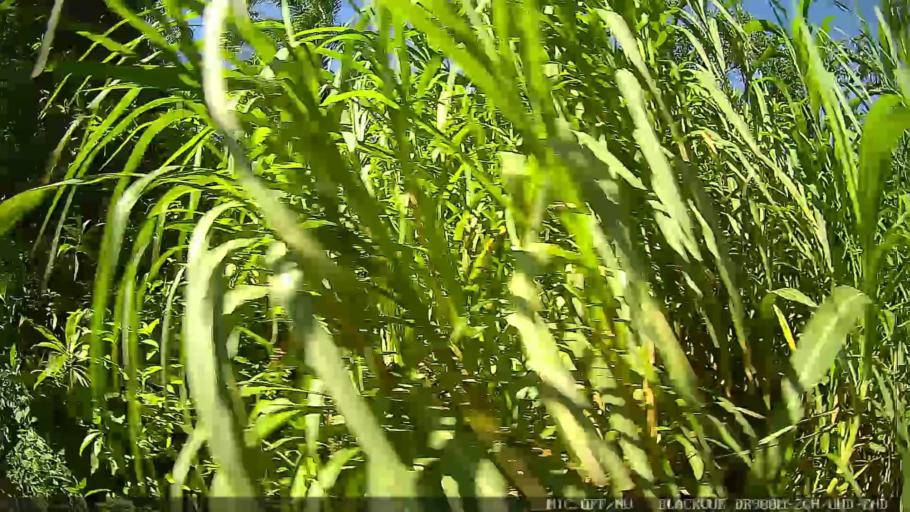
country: BR
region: Sao Paulo
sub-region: Iguape
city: Iguape
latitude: -24.6989
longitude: -47.5598
